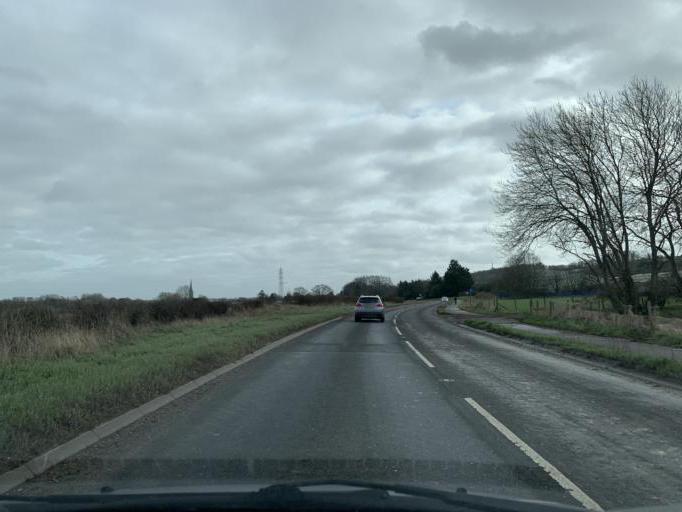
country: GB
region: England
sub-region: Wiltshire
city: Salisbury
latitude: 51.0628
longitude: -1.8293
